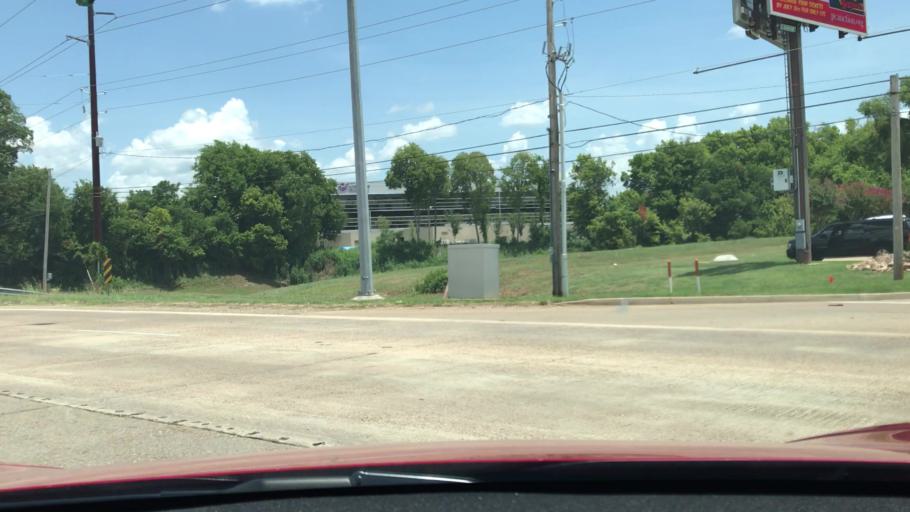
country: US
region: Louisiana
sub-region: Bossier Parish
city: Bossier City
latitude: 32.4235
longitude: -93.7201
